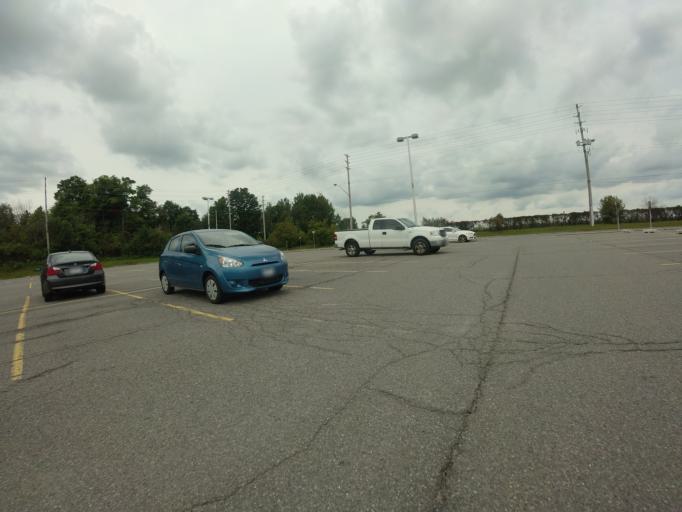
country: CA
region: Quebec
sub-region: Outaouais
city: Gatineau
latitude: 45.4803
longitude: -75.5203
